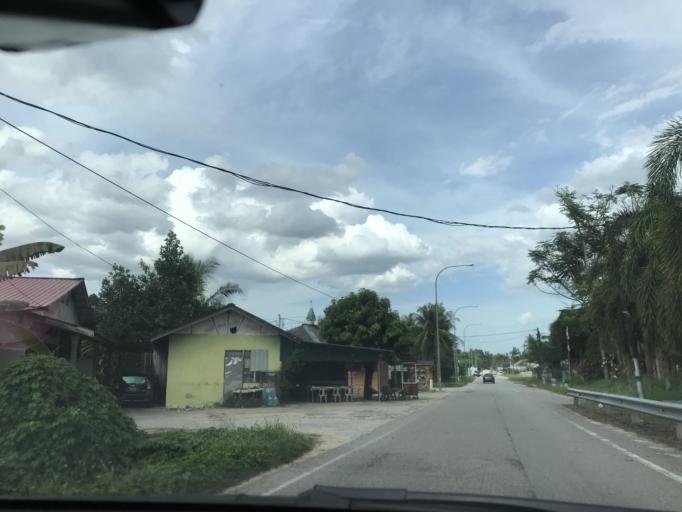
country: MY
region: Kelantan
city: Kampung Lemal
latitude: 6.0338
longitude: 102.1593
